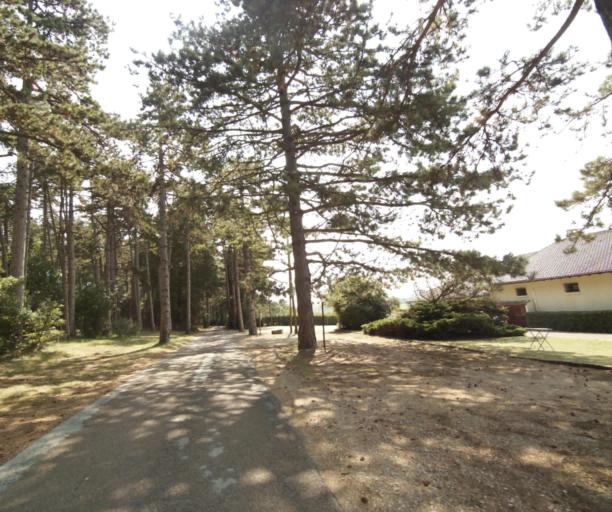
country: FR
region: Bourgogne
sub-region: Departement de Saone-et-Loire
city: Tournus
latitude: 46.5811
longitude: 4.8924
